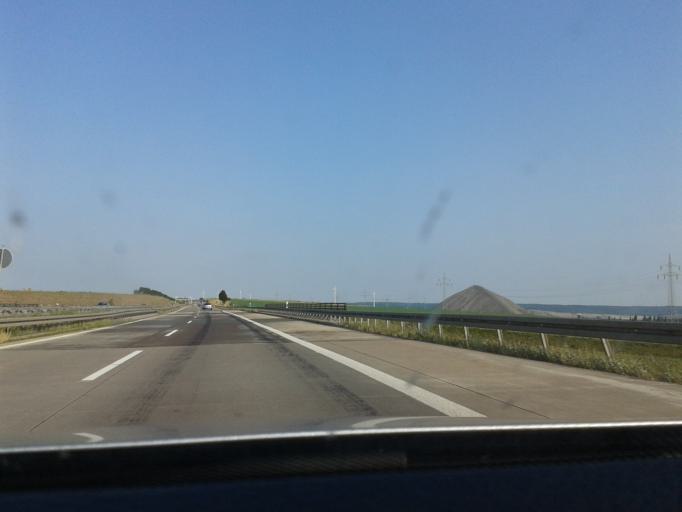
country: DE
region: Saxony-Anhalt
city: Oberroblingen
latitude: 51.4411
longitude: 11.3325
